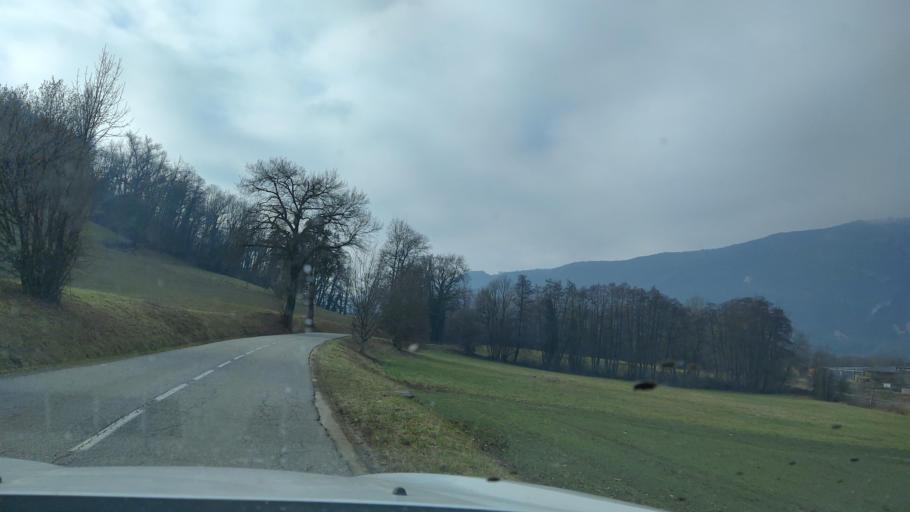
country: FR
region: Rhone-Alpes
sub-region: Departement de la Savoie
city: La Biolle
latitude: 45.7493
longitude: 5.9390
